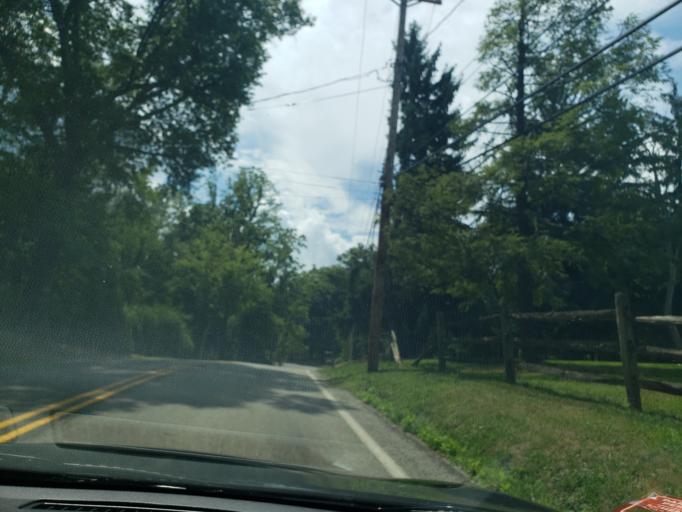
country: US
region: Pennsylvania
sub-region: Allegheny County
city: Coraopolis
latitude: 40.5420
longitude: -80.1449
